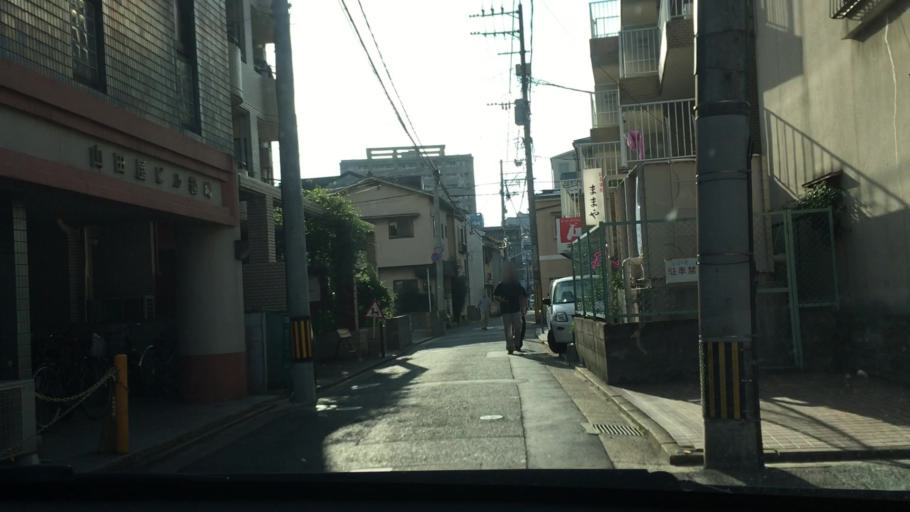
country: JP
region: Fukuoka
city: Fukuoka-shi
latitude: 33.6193
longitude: 130.4204
